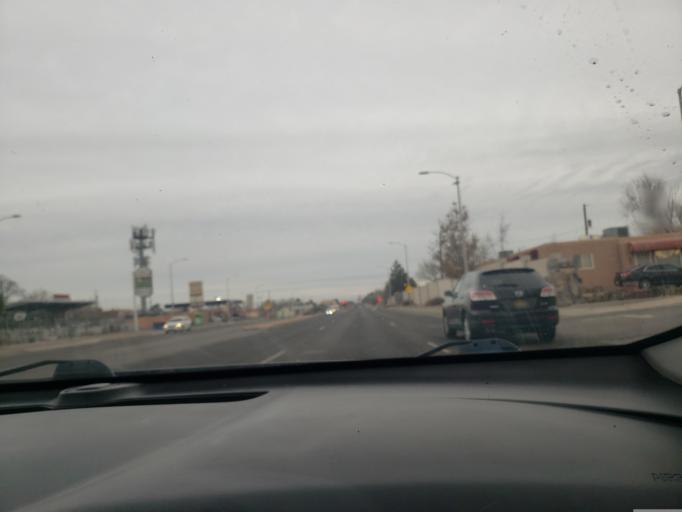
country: US
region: New Mexico
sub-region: Bernalillo County
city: Albuquerque
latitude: 35.0926
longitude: -106.5862
